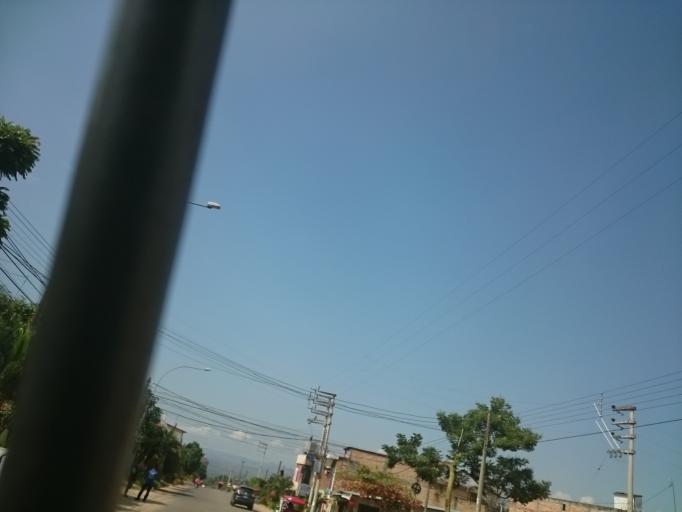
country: PE
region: San Martin
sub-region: Provincia de San Martin
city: Tarapoto
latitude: -6.4745
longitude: -76.3726
